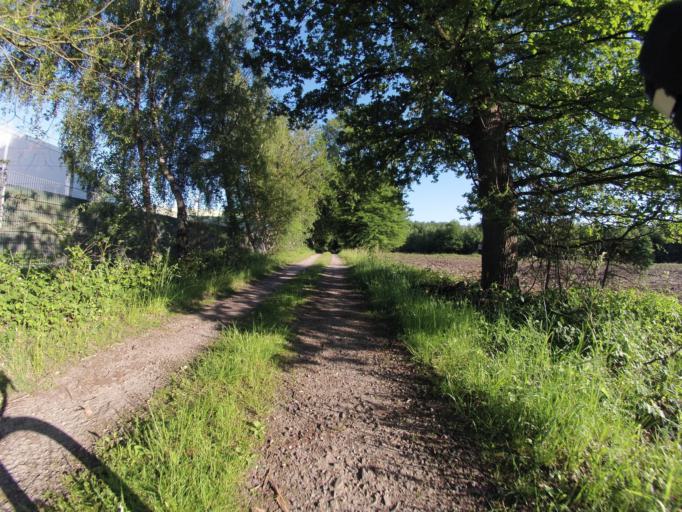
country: DE
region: Lower Saxony
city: Bad Bentheim
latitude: 52.3119
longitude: 7.1347
